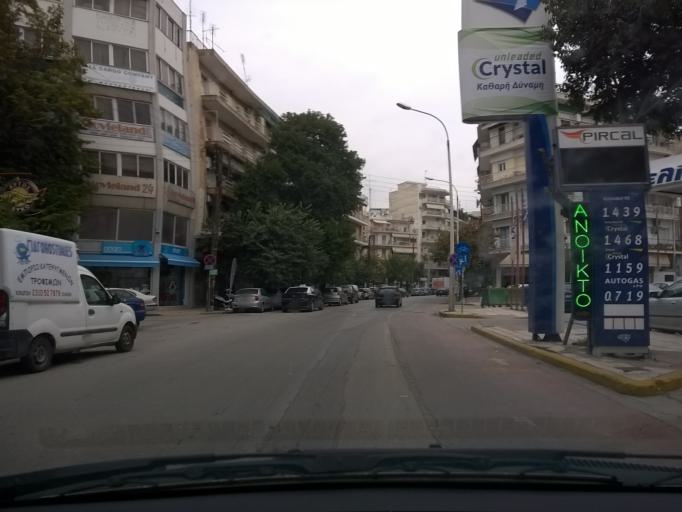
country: GR
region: Central Macedonia
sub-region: Nomos Thessalonikis
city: Thessaloniki
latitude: 40.6414
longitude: 22.9286
